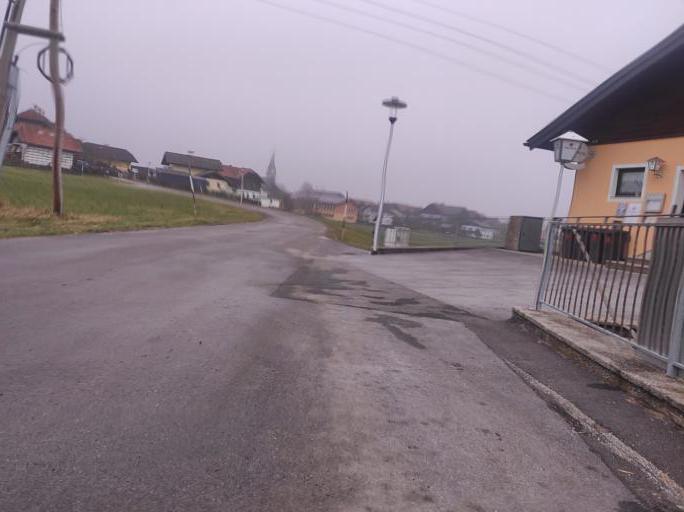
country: AT
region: Salzburg
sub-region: Politischer Bezirk Salzburg-Umgebung
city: Schleedorf
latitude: 47.9521
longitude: 13.1569
